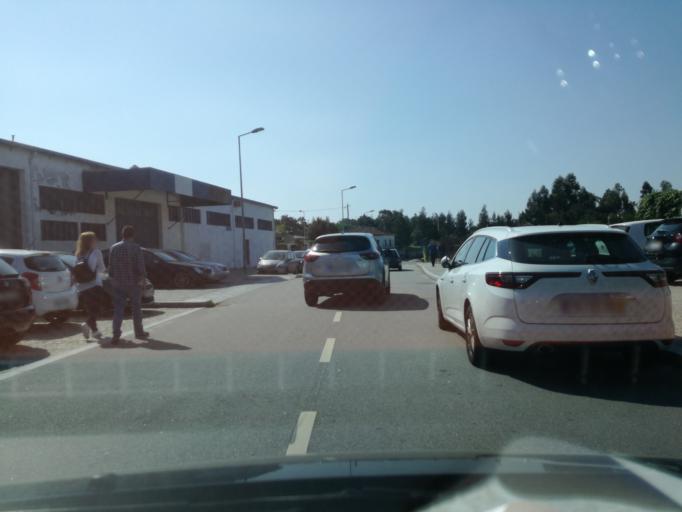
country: PT
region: Porto
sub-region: Maia
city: Maia
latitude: 41.2339
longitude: -8.6335
